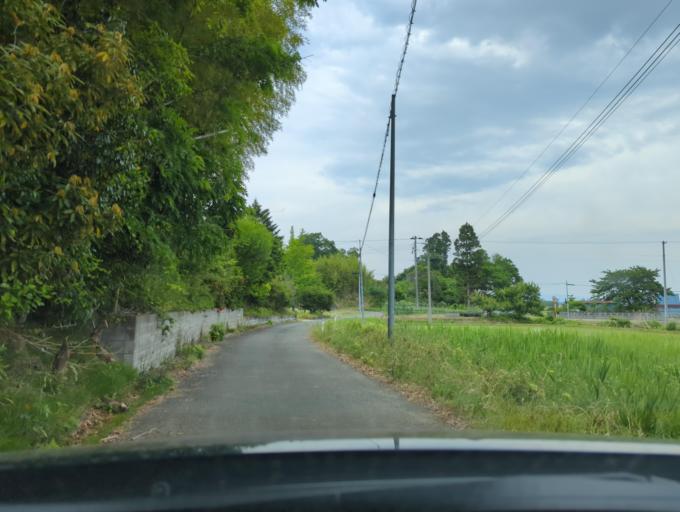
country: JP
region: Fukushima
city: Koriyama
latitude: 37.3752
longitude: 140.3001
